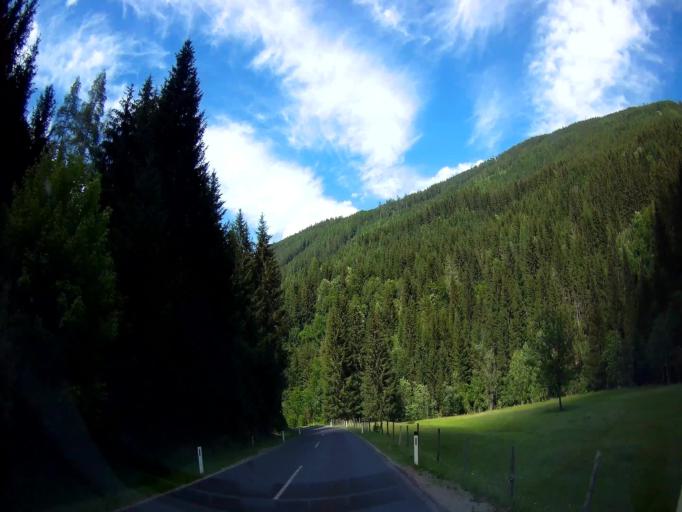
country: AT
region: Styria
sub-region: Politischer Bezirk Murau
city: Stadl an der Mur
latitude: 47.0468
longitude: 14.0001
